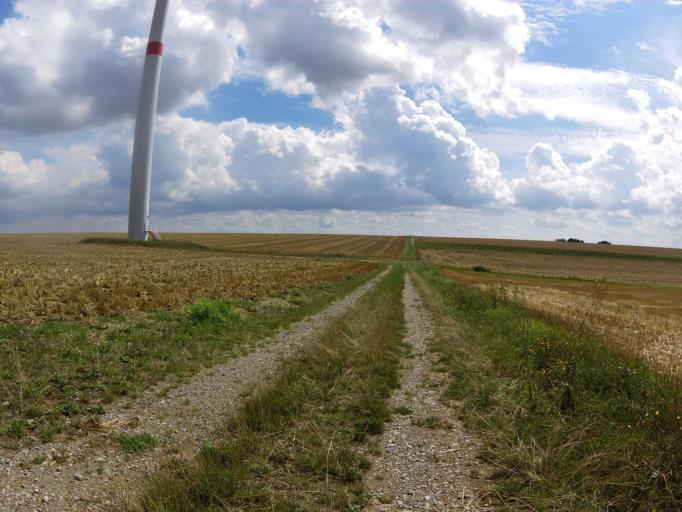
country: DE
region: Bavaria
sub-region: Regierungsbezirk Unterfranken
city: Geroldshausen
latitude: 49.6969
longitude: 9.8935
